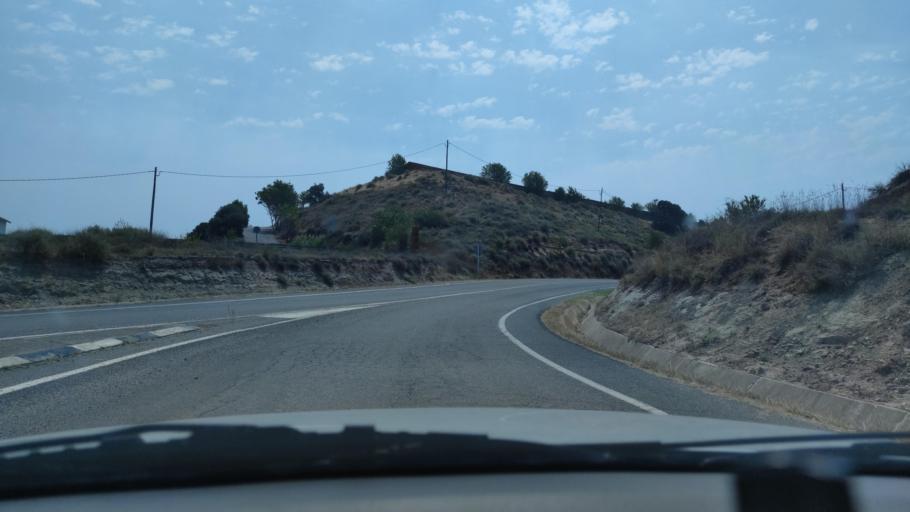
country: ES
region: Catalonia
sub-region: Provincia de Lleida
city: Bellpuig
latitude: 41.6113
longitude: 1.0306
